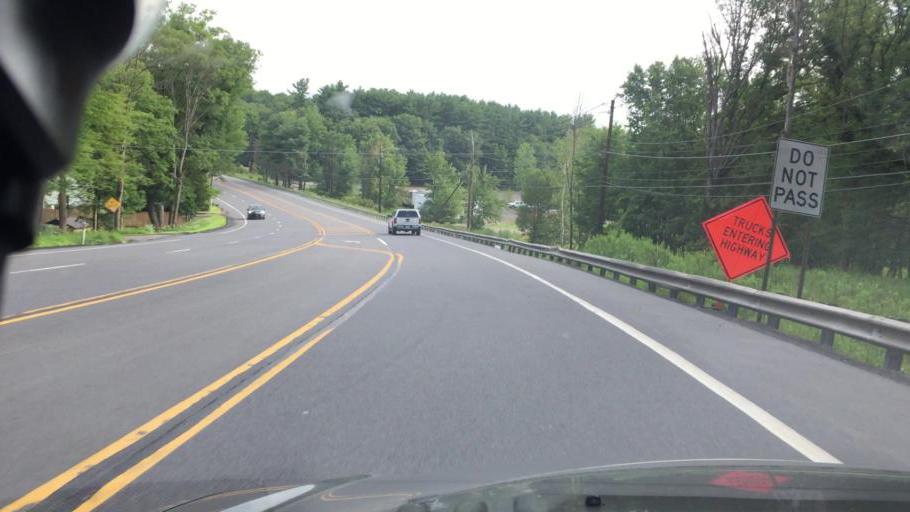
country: US
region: Pennsylvania
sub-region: Luzerne County
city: Oakdale
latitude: 41.0337
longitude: -75.9523
